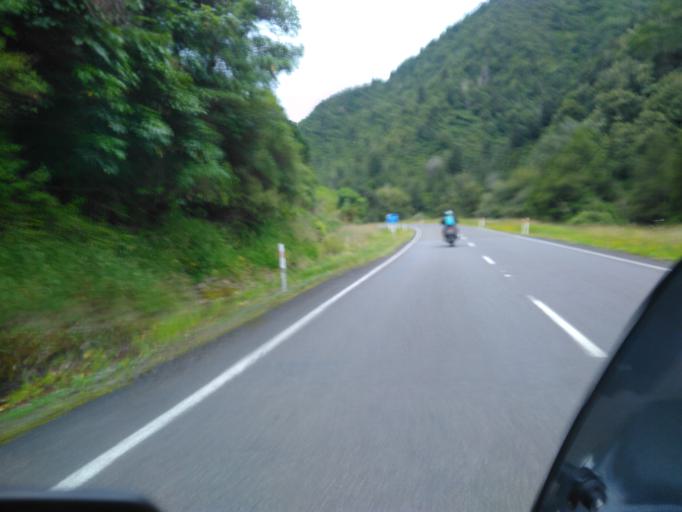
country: NZ
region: Bay of Plenty
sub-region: Opotiki District
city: Opotiki
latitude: -38.2904
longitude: 177.3817
